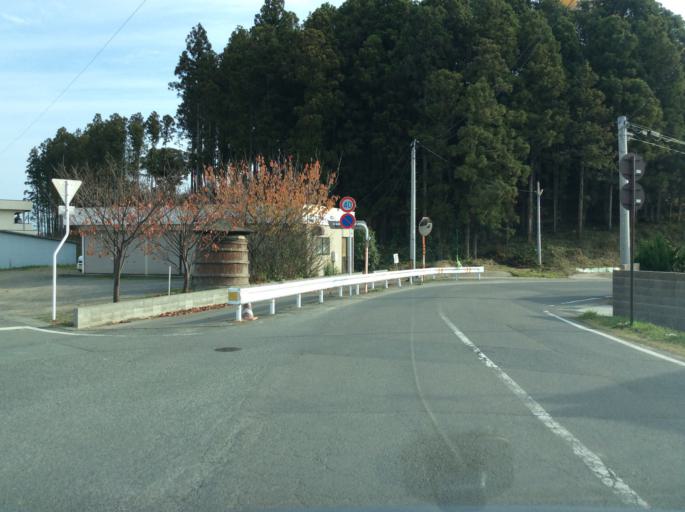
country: JP
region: Fukushima
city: Iwaki
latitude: 37.0705
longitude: 140.9426
